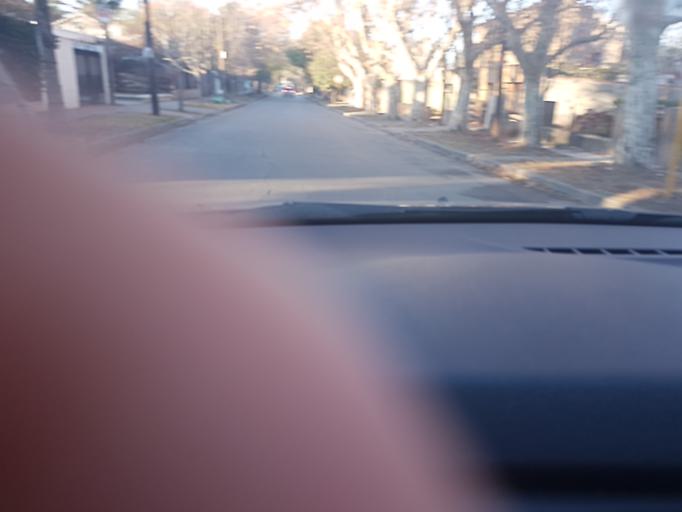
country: AR
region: Cordoba
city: Villa Allende
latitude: -31.3464
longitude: -64.2522
